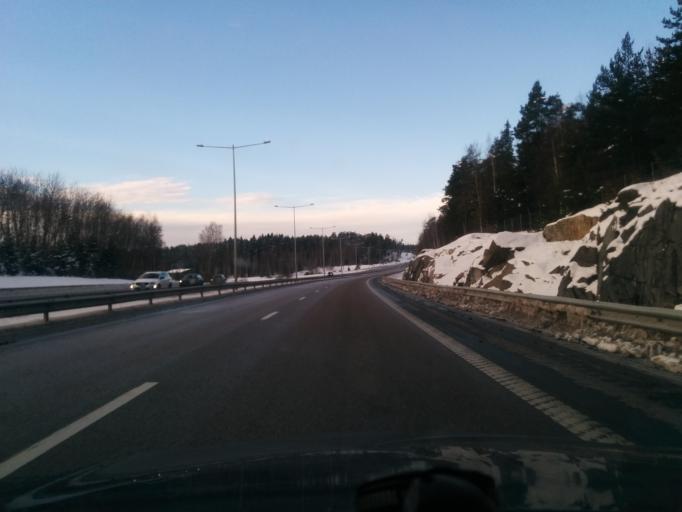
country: SE
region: Stockholm
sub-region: Upplands-Bro Kommun
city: Bro
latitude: 59.5284
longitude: 17.6368
